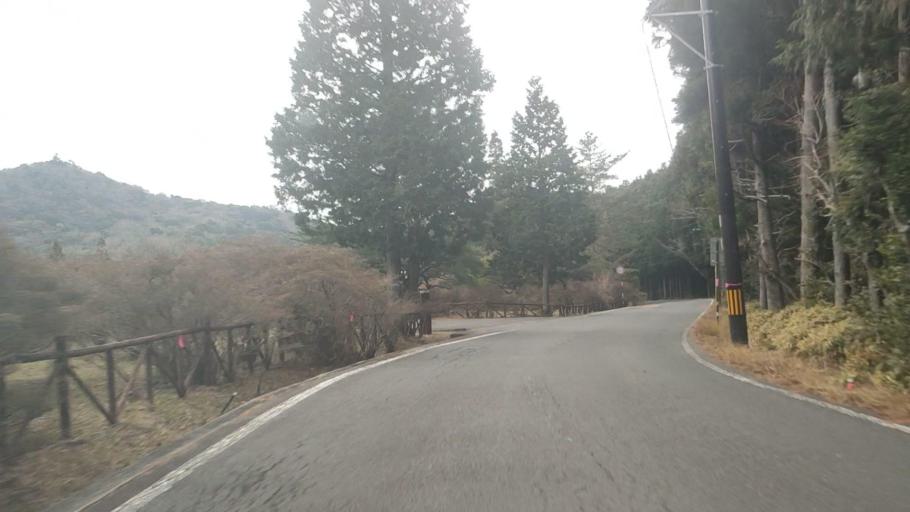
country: JP
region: Nagasaki
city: Shimabara
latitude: 32.7460
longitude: 130.2704
